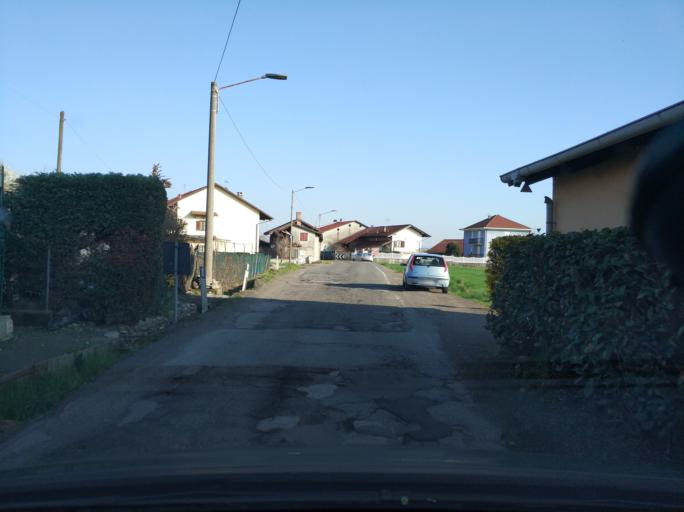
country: IT
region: Piedmont
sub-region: Provincia di Torino
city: Cirie
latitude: 45.2026
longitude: 7.6022
